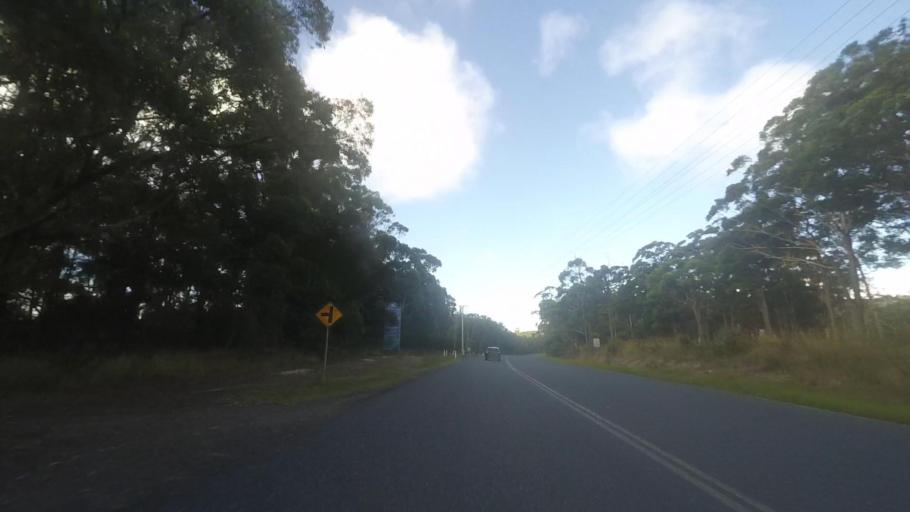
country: AU
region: New South Wales
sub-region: Great Lakes
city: Forster
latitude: -32.3560
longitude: 152.5051
